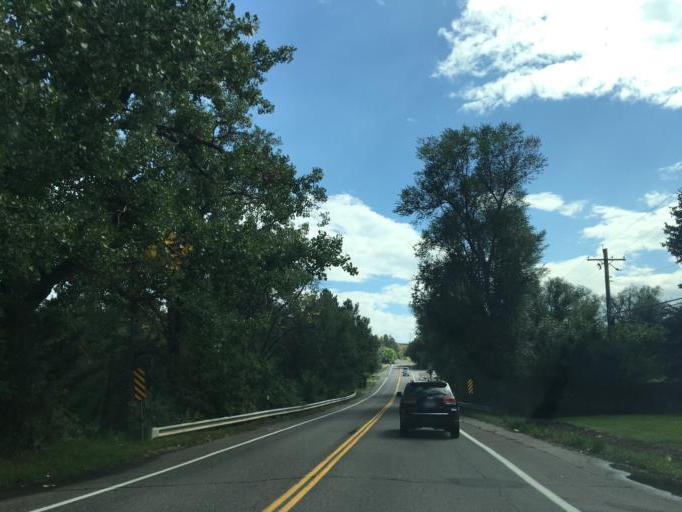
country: US
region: Colorado
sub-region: Jefferson County
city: Applewood
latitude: 39.7441
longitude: -105.1424
